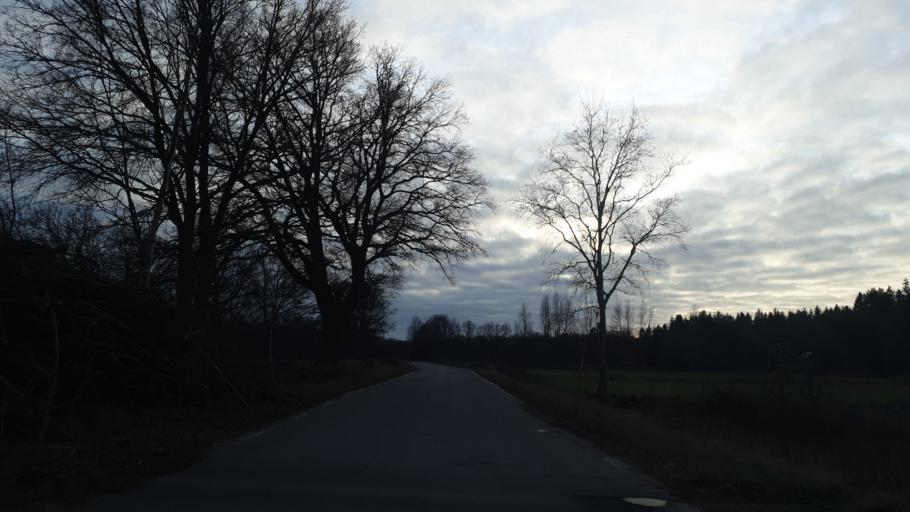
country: SE
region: Blekinge
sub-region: Karlskrona Kommun
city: Jaemjoe
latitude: 56.1812
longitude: 15.9376
